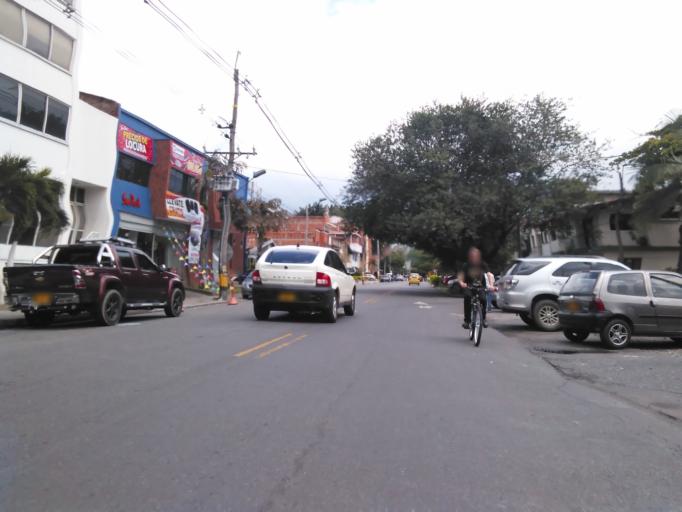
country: CO
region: Antioquia
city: Medellin
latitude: 6.2387
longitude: -75.5864
